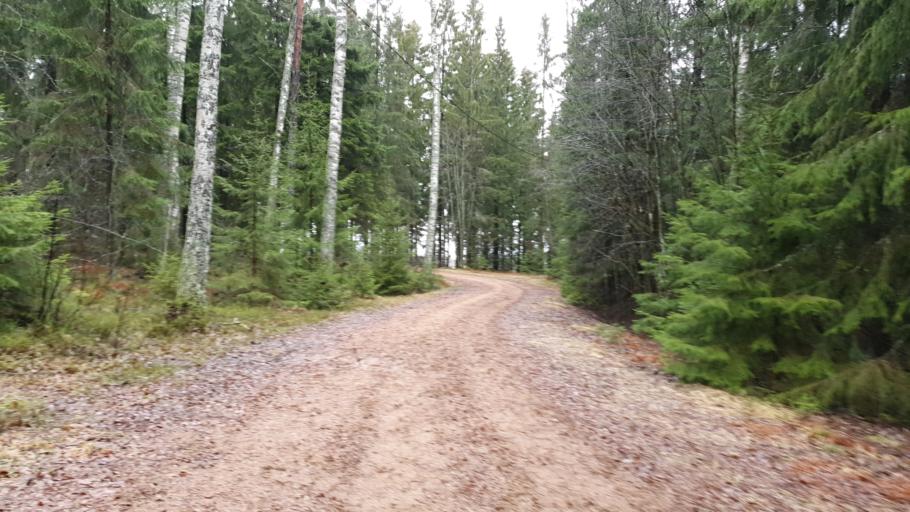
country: FI
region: Uusimaa
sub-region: Helsinki
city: Helsinki
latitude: 60.2697
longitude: 24.9191
